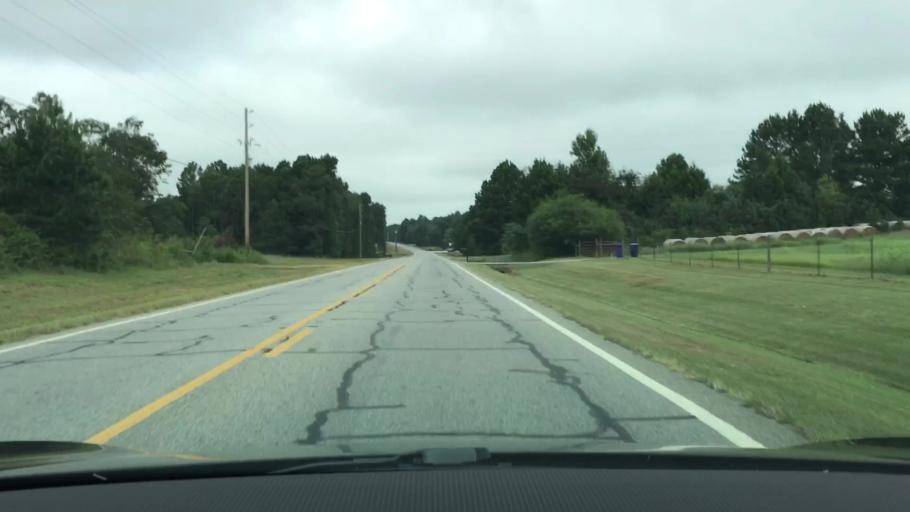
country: US
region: Georgia
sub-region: Oconee County
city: Watkinsville
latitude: 33.8040
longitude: -83.3429
